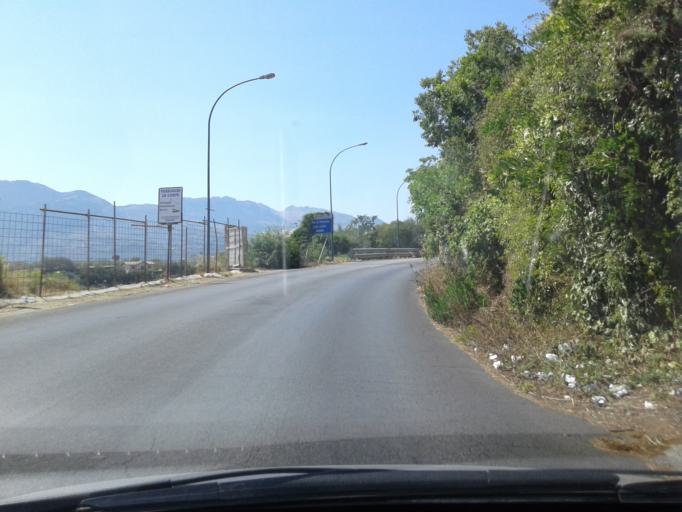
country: IT
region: Sicily
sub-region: Palermo
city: Cannizzaro-Favara
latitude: 38.0727
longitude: 13.2771
